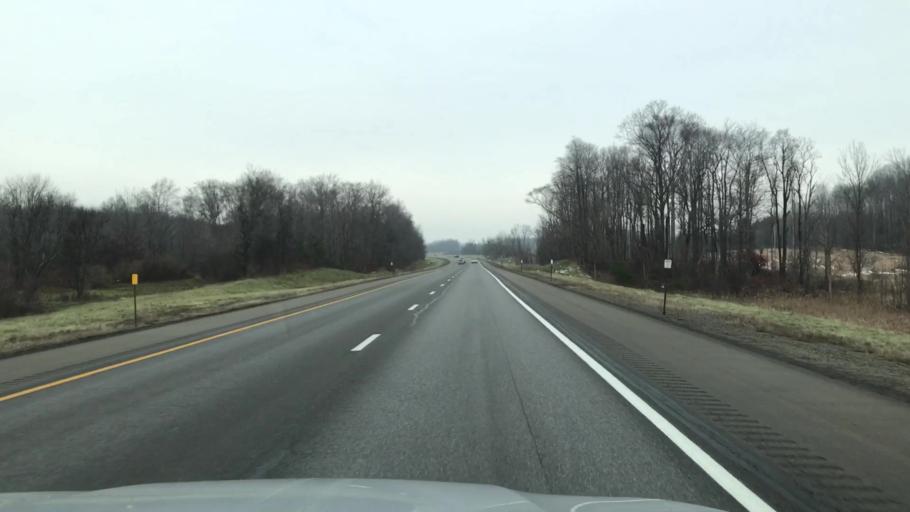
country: US
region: New York
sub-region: Erie County
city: Lake Erie Beach
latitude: 42.5946
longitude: -79.0448
